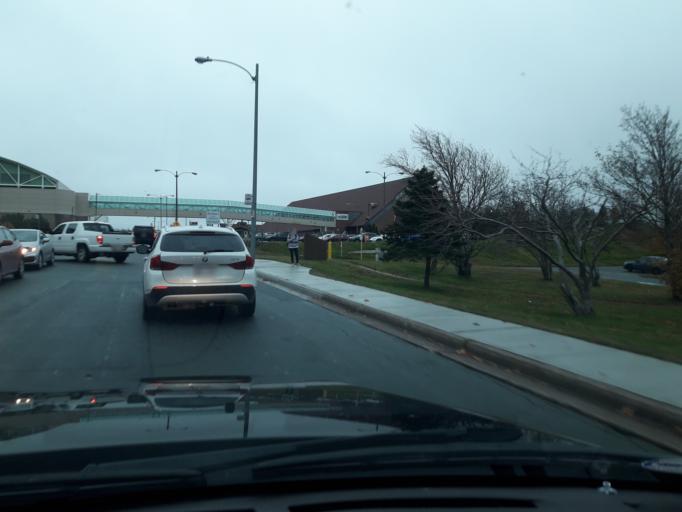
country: CA
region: Newfoundland and Labrador
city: St. John's
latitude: 47.5709
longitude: -52.7371
